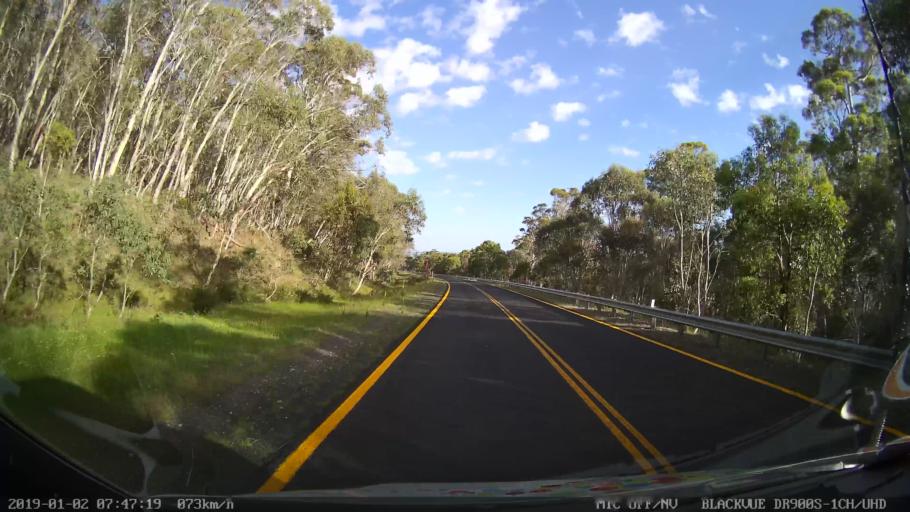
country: AU
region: New South Wales
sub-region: Tumut Shire
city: Tumut
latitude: -35.7659
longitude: 148.5213
